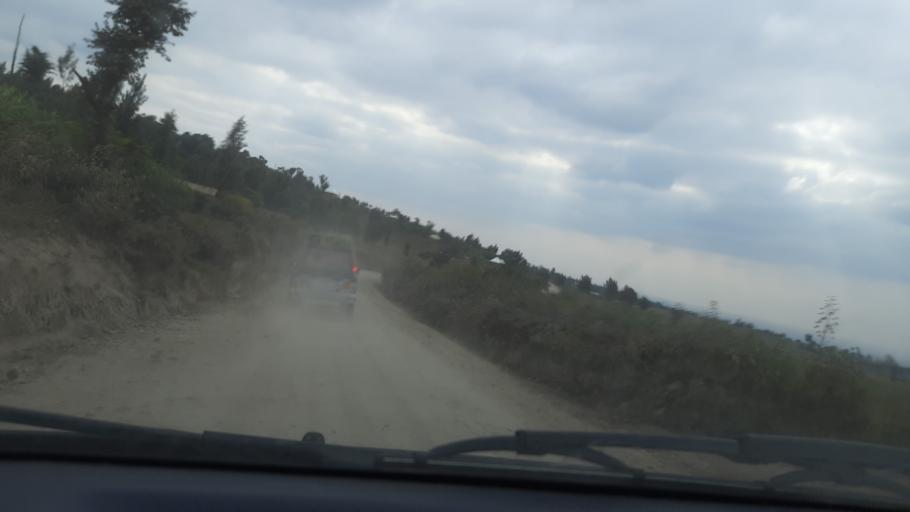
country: TZ
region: Kilimanjaro
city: Moshi
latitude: -2.8758
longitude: 37.3594
